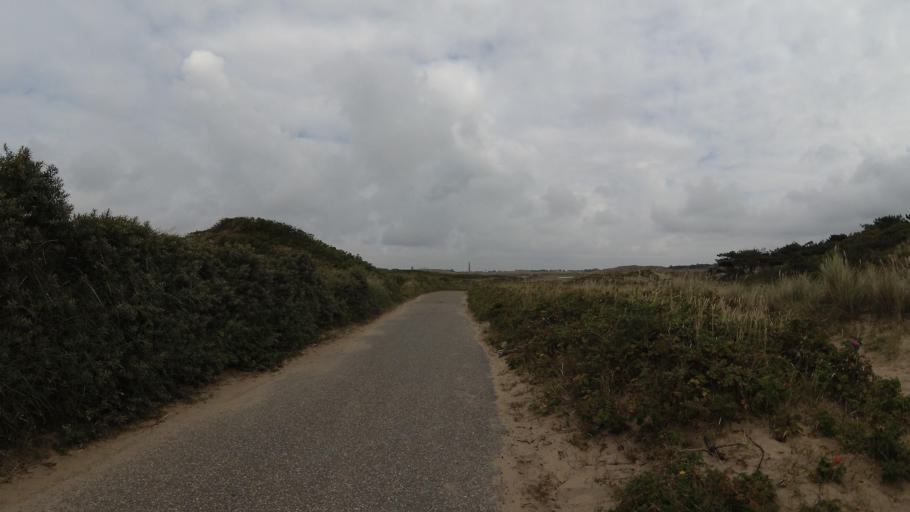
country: NL
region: North Holland
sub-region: Gemeente Den Helder
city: Den Helder
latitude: 52.9380
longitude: 4.7184
